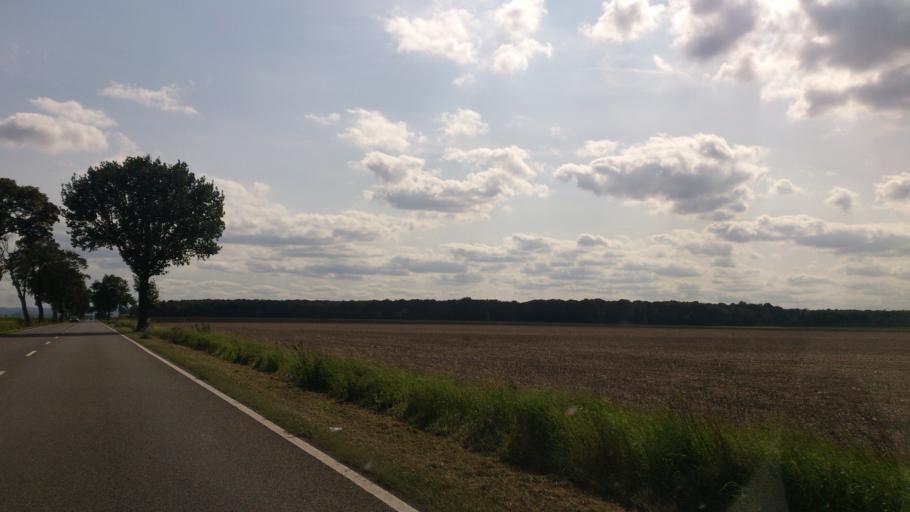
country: DE
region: North Rhine-Westphalia
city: Zulpich
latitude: 50.7397
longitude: 6.7067
